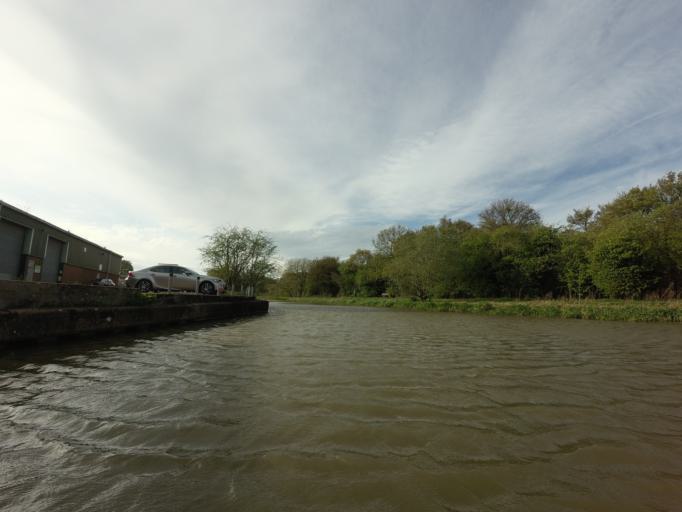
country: GB
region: England
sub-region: Milton Keynes
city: Stony Stratford
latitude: 52.0656
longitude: -0.8277
